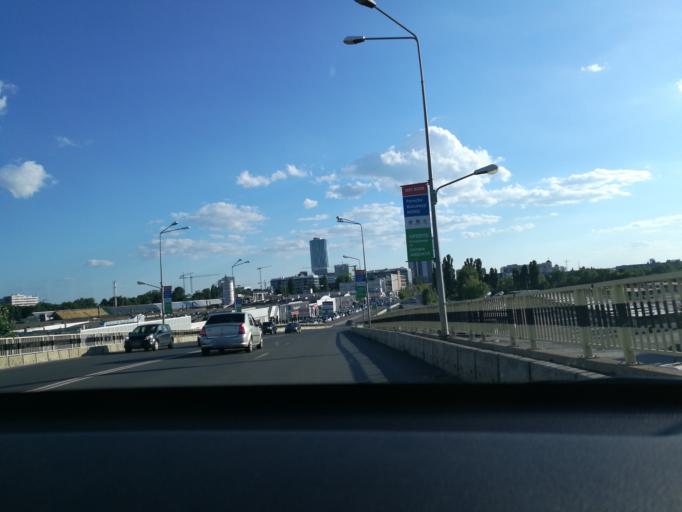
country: RO
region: Bucuresti
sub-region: Municipiul Bucuresti
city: Bucharest
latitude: 44.4867
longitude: 26.1138
